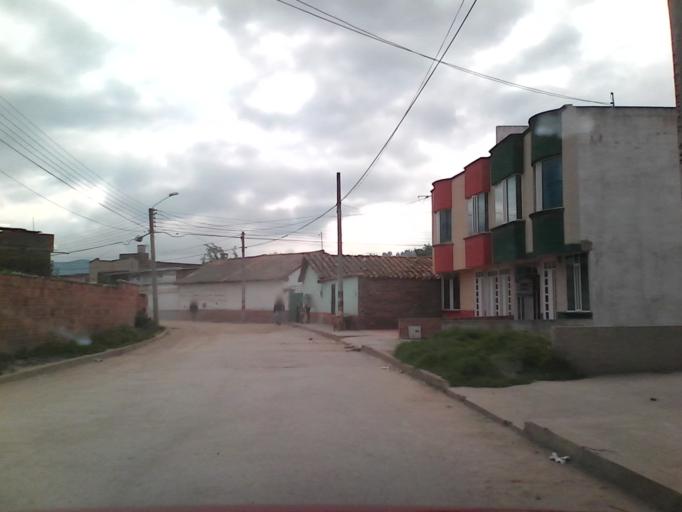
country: CO
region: Boyaca
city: Duitama
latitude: 5.8129
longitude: -73.0249
